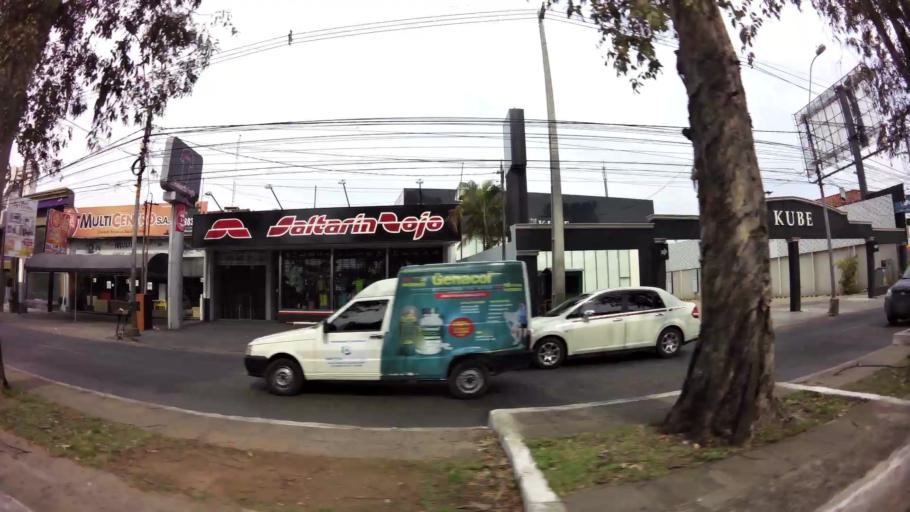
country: PY
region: Asuncion
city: Asuncion
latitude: -25.2890
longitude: -57.5733
